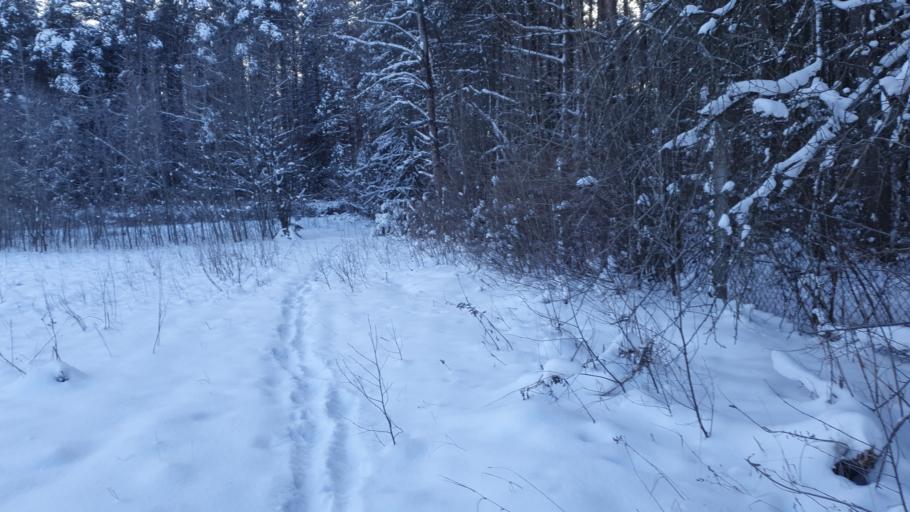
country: LT
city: Skaidiskes
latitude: 54.6469
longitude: 25.4216
